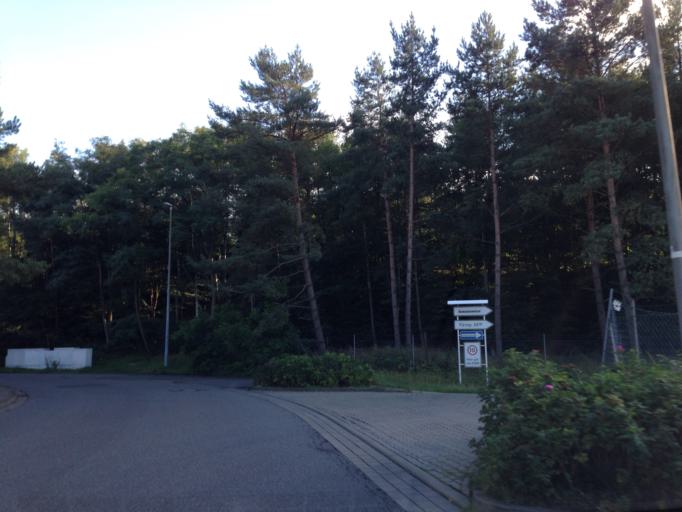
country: DE
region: Lower Saxony
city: Wendisch Evern
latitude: 53.2377
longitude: 10.4793
